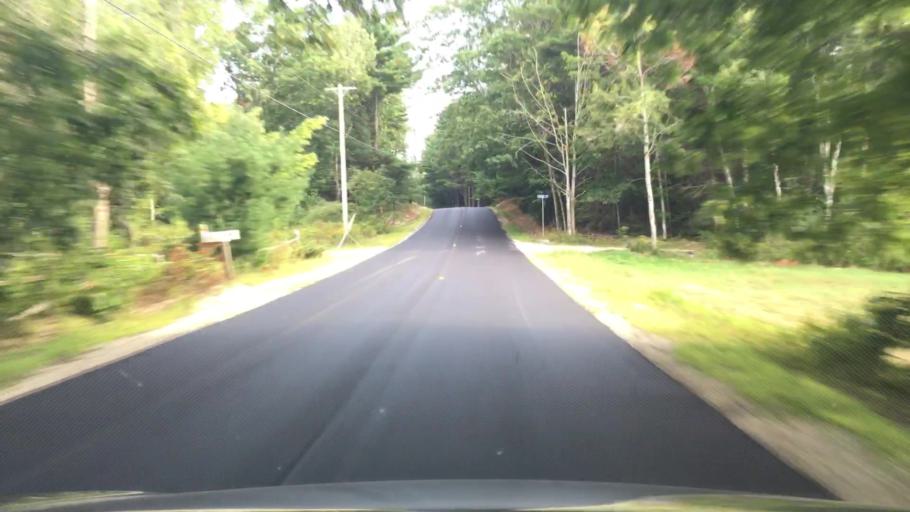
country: US
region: Maine
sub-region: Hancock County
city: Surry
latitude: 44.5247
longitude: -68.6093
